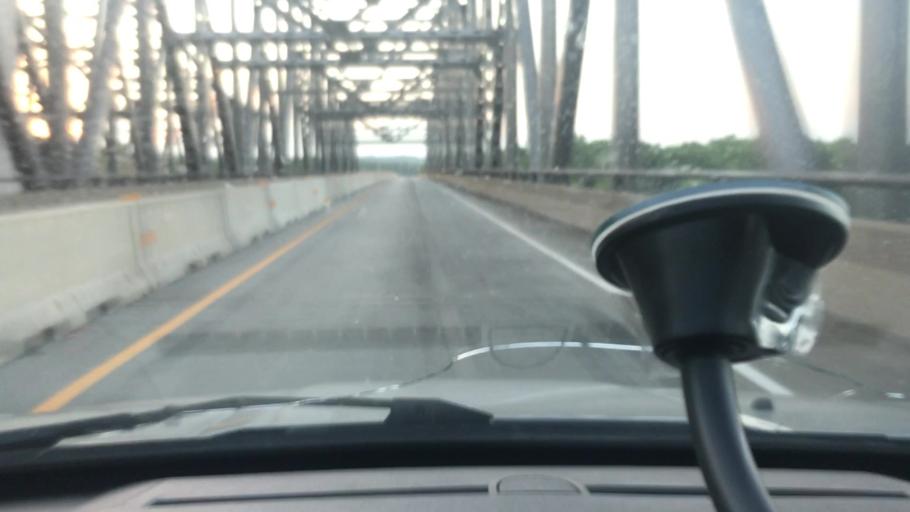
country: US
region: Illinois
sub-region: Tazewell County
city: North Pekin
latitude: 40.6351
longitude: -89.6223
